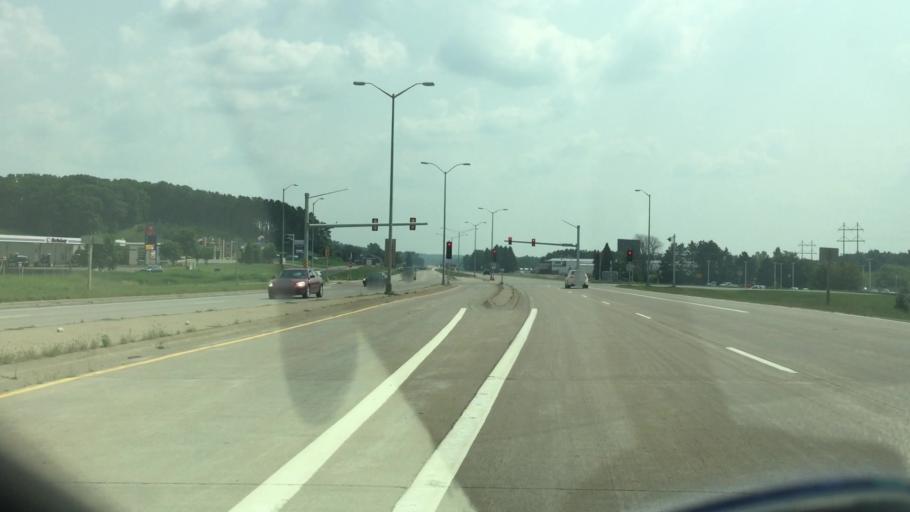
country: US
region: Wisconsin
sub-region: Eau Claire County
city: Altoona
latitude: 44.7626
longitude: -91.4589
